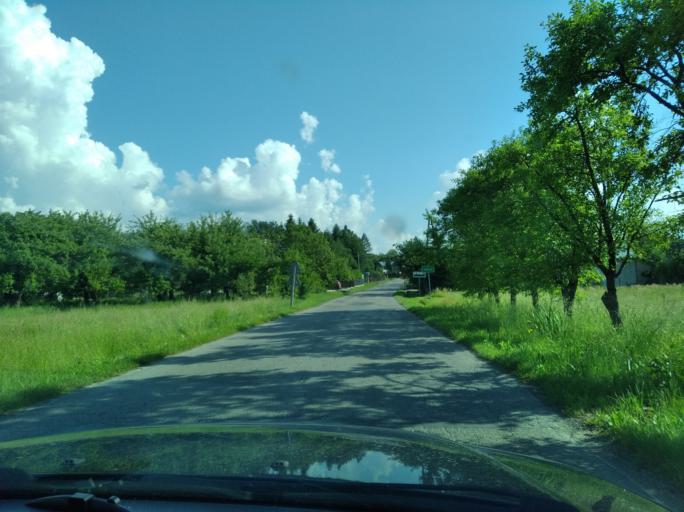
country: PL
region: Subcarpathian Voivodeship
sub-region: Powiat jaroslawski
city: Kramarzowka
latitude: 49.8490
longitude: 22.5159
